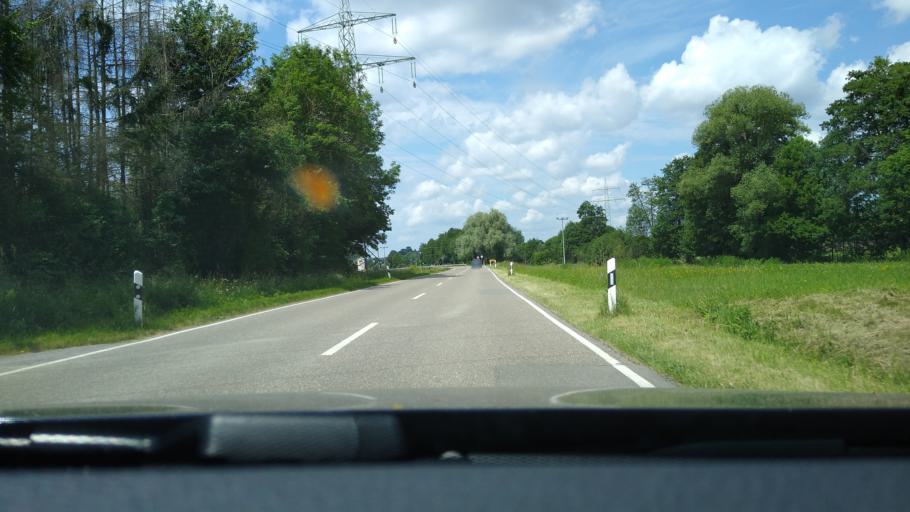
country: DE
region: Bavaria
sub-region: Regierungsbezirk Mittelfranken
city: Obernzenn
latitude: 49.4533
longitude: 10.4893
